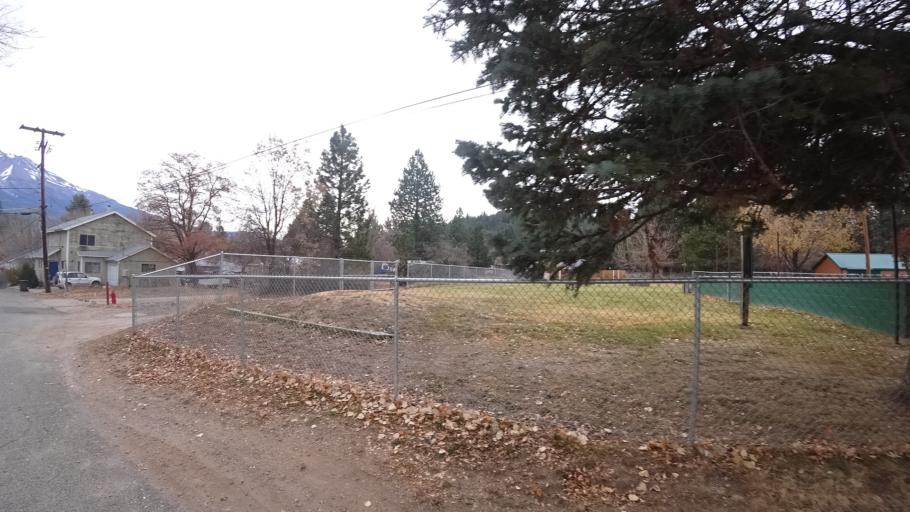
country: US
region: California
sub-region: Siskiyou County
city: Weed
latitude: 41.4153
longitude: -122.3871
